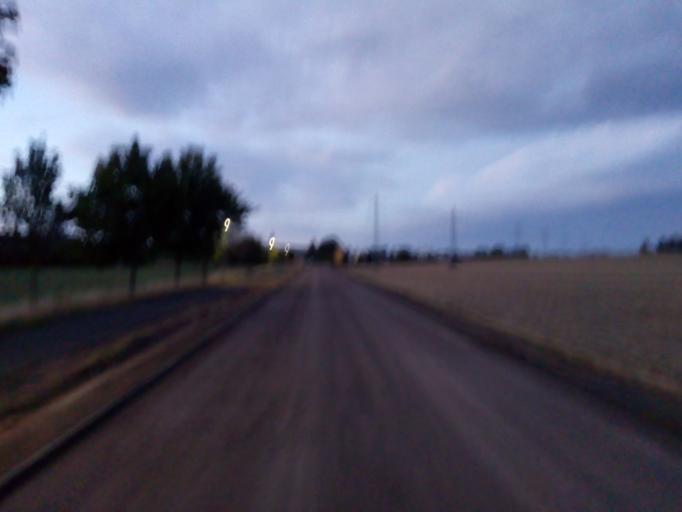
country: DE
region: Rheinland-Pfalz
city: Waldalgesheim
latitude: 49.9438
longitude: 7.8254
